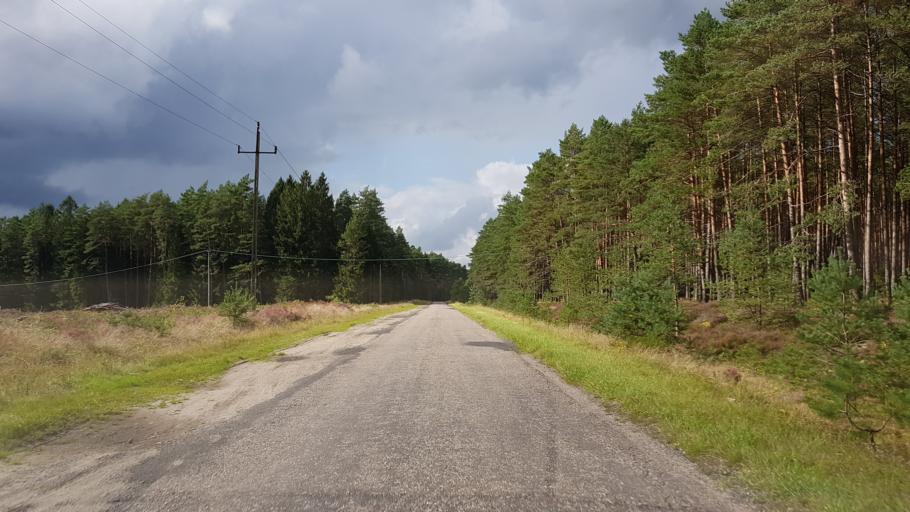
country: PL
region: West Pomeranian Voivodeship
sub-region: Powiat bialogardzki
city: Tychowo
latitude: 54.0429
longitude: 16.3195
